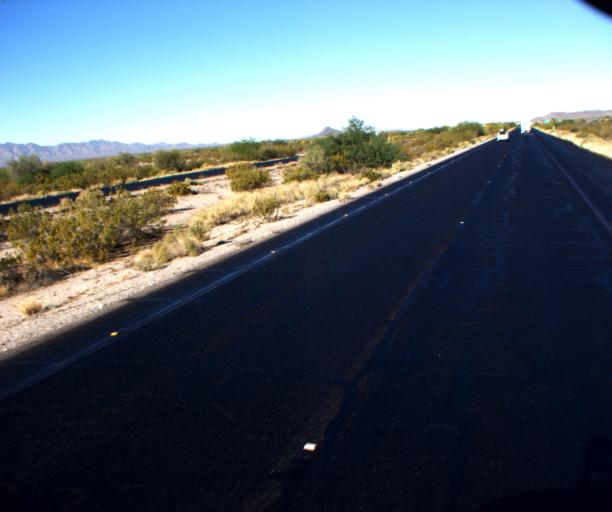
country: US
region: Arizona
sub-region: Pinal County
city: Maricopa
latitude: 32.8411
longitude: -112.2456
